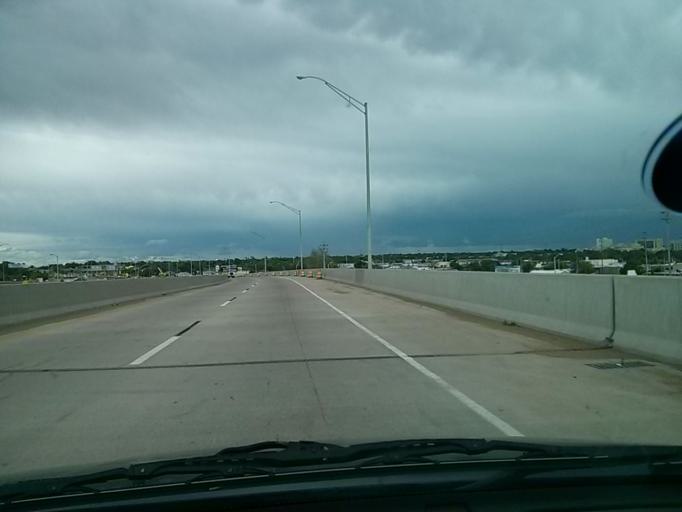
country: US
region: Oklahoma
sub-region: Tulsa County
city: Tulsa
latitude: 36.1595
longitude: -95.9816
